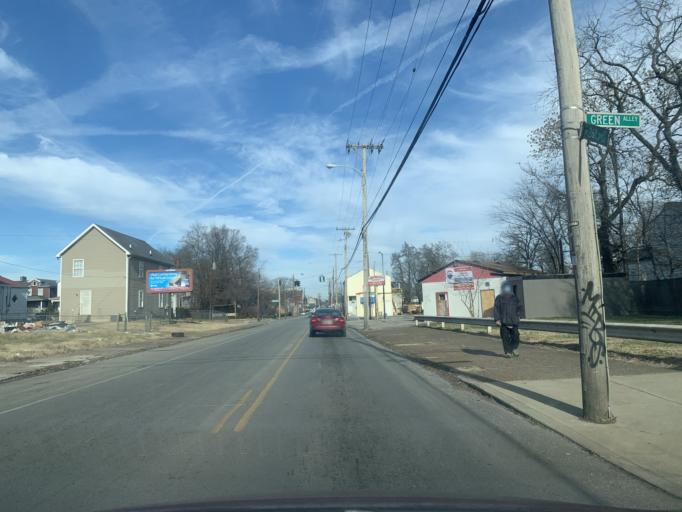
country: US
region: Kentucky
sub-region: Jefferson County
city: Louisville
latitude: 38.2572
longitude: -85.7940
